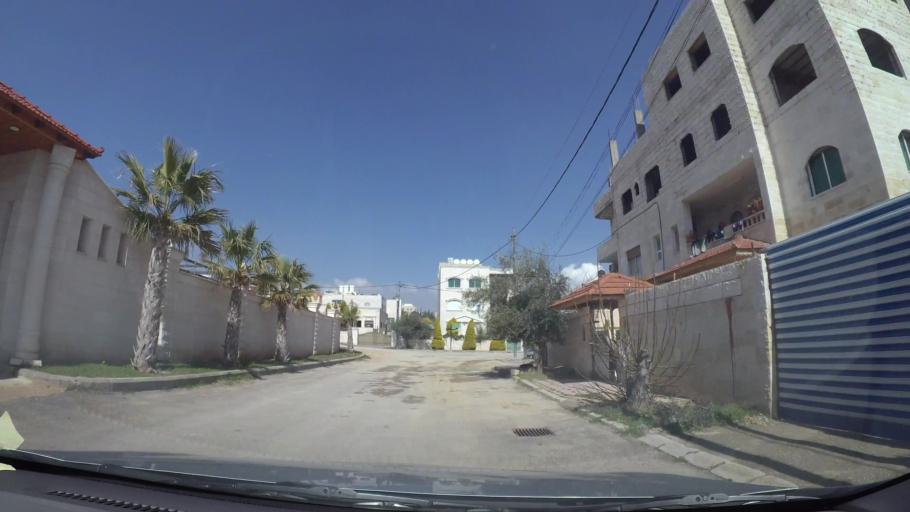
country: JO
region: Amman
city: Al Bunayyat ash Shamaliyah
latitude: 31.9019
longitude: 35.8961
